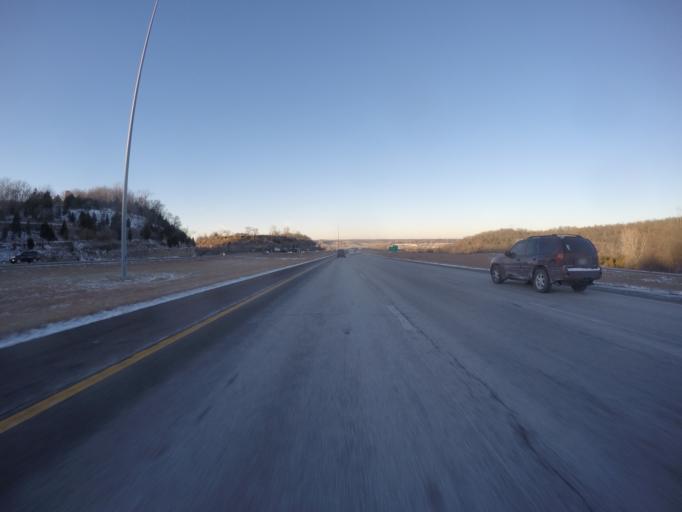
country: US
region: Kansas
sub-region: Wyandotte County
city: Edwardsville
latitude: 39.0379
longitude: -94.7885
